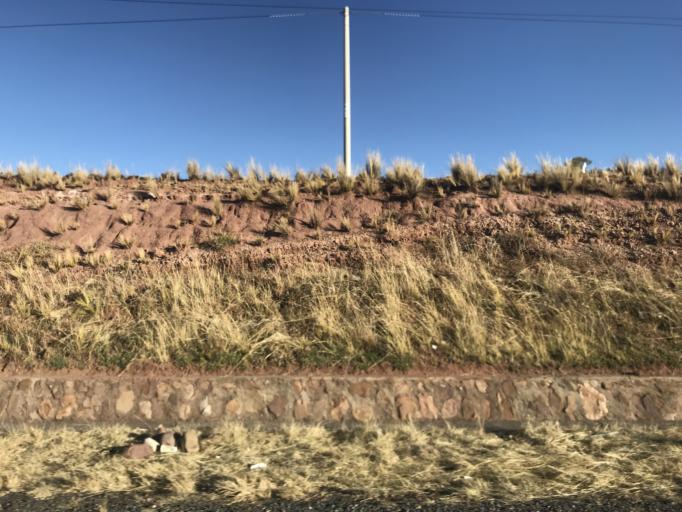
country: BO
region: La Paz
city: Tiahuanaco
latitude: -16.5654
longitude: -68.6404
